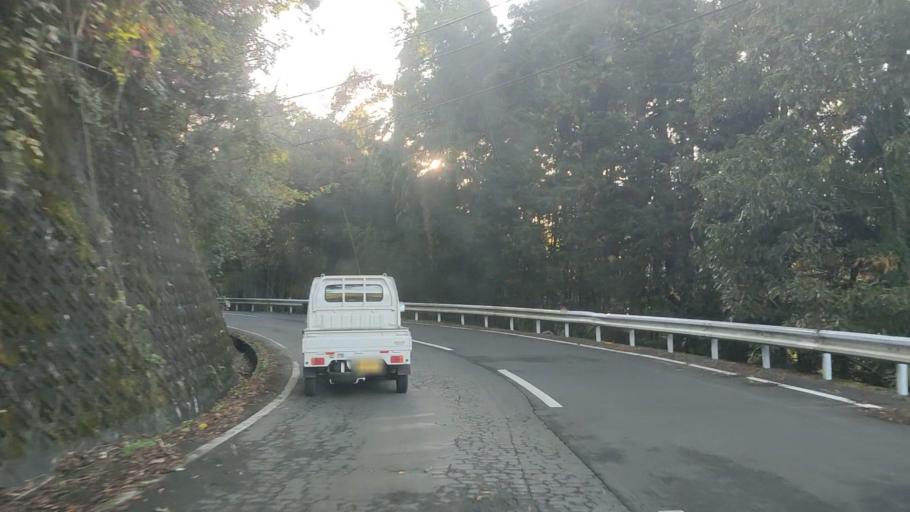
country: JP
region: Shizuoka
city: Mishima
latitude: 35.1336
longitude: 138.9694
